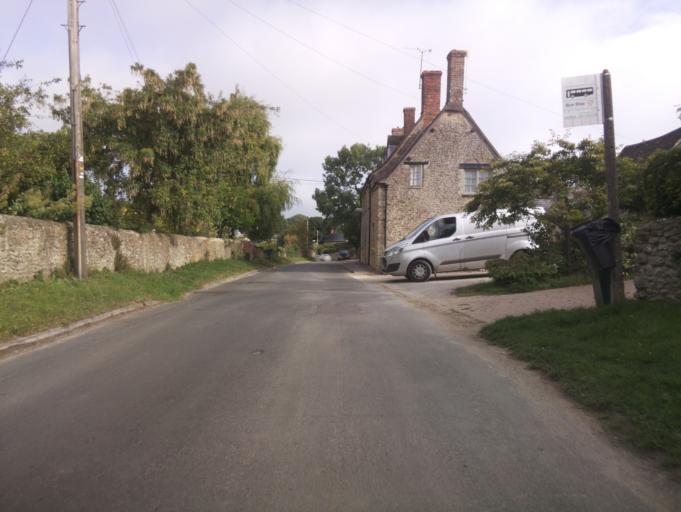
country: GB
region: England
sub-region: Borough of Swindon
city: Hannington
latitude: 51.6114
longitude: -1.7445
